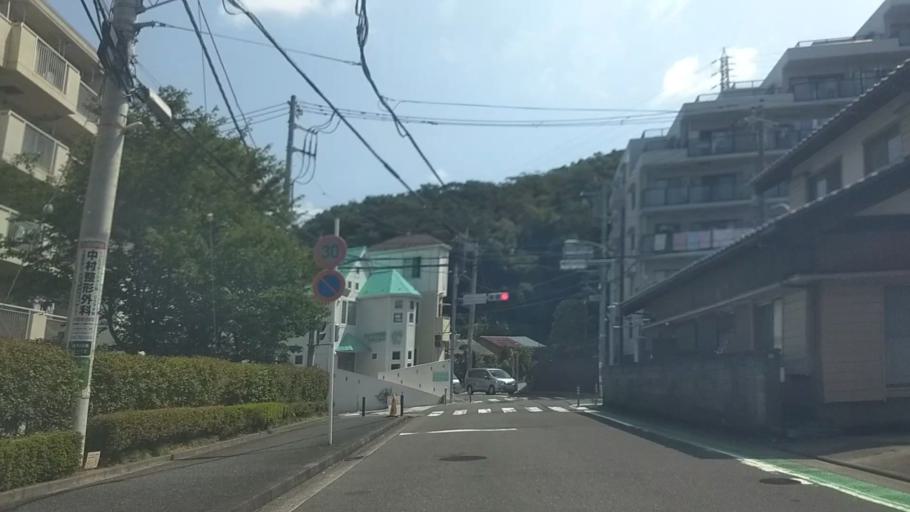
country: JP
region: Kanagawa
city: Zushi
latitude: 35.3362
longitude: 139.6084
